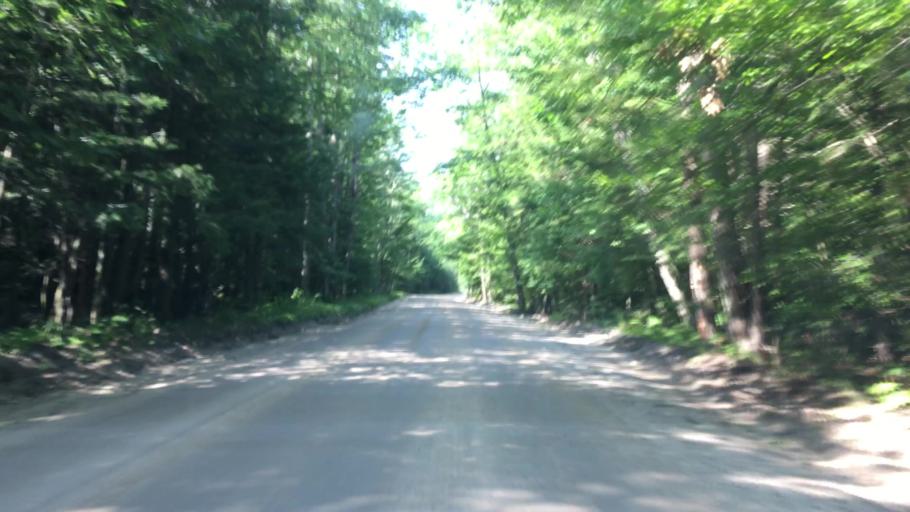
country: US
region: Maine
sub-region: Androscoggin County
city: Poland
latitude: 43.9900
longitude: -70.3742
